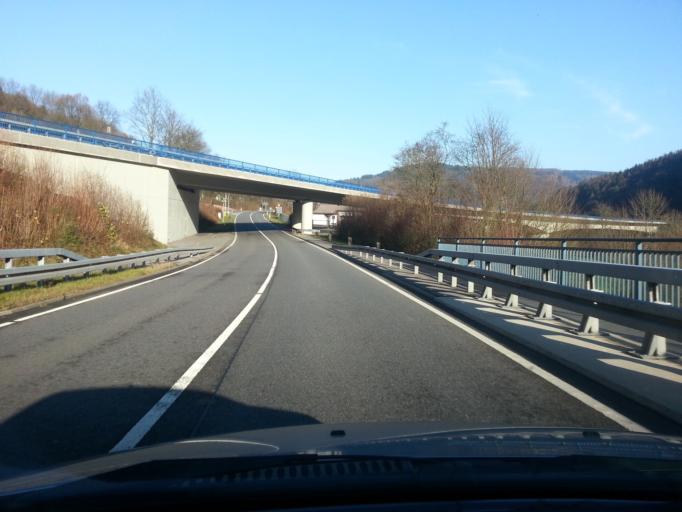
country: DE
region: Hesse
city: Hirschhorn
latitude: 49.4358
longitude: 8.8958
